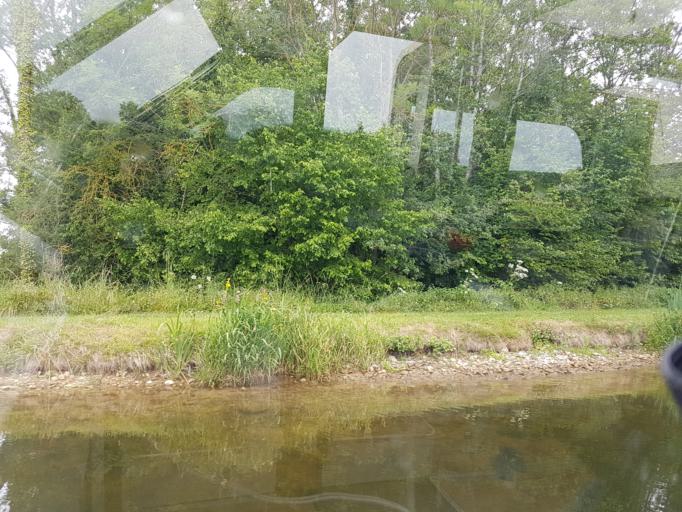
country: FR
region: Bourgogne
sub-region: Departement de l'Yonne
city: Moneteau
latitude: 47.8421
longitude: 3.5754
